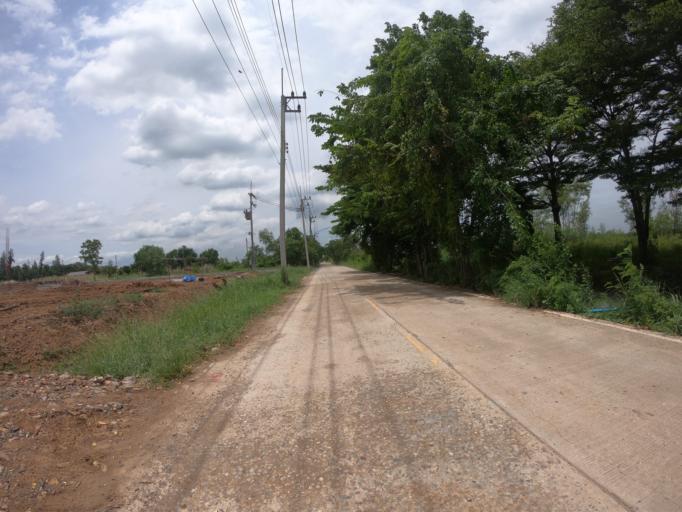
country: TH
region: Pathum Thani
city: Ban Lam Luk Ka
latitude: 13.9901
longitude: 100.8590
